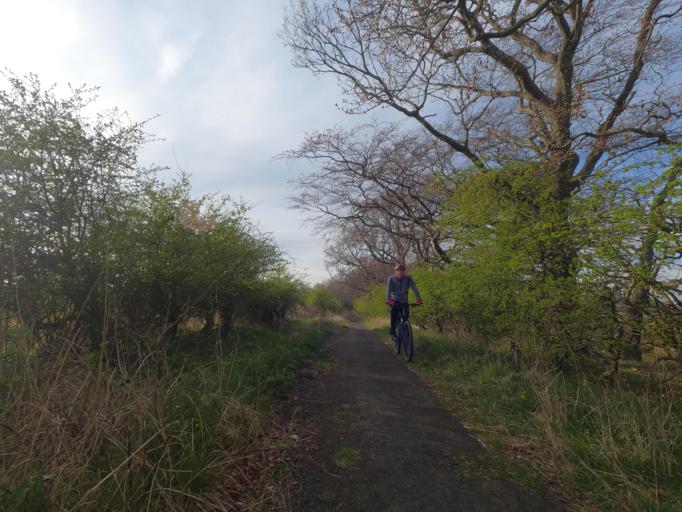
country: GB
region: England
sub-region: Northumberland
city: Cramlington
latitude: 55.0736
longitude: -1.6044
